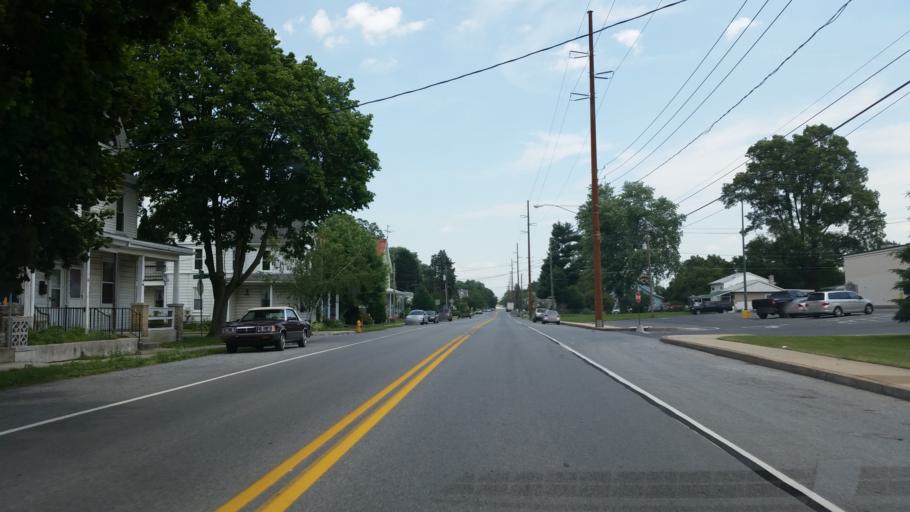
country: US
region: Pennsylvania
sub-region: Dauphin County
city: Steelton
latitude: 40.2241
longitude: -76.8588
